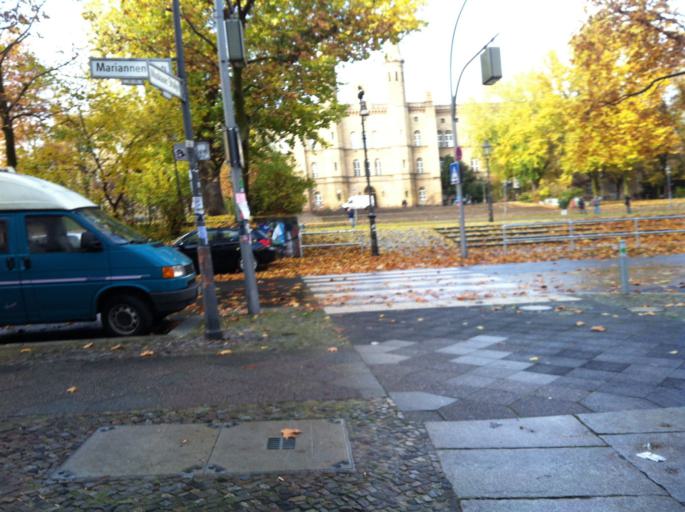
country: DE
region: Berlin
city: Berlin Treptow
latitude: 52.5033
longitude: 13.4262
